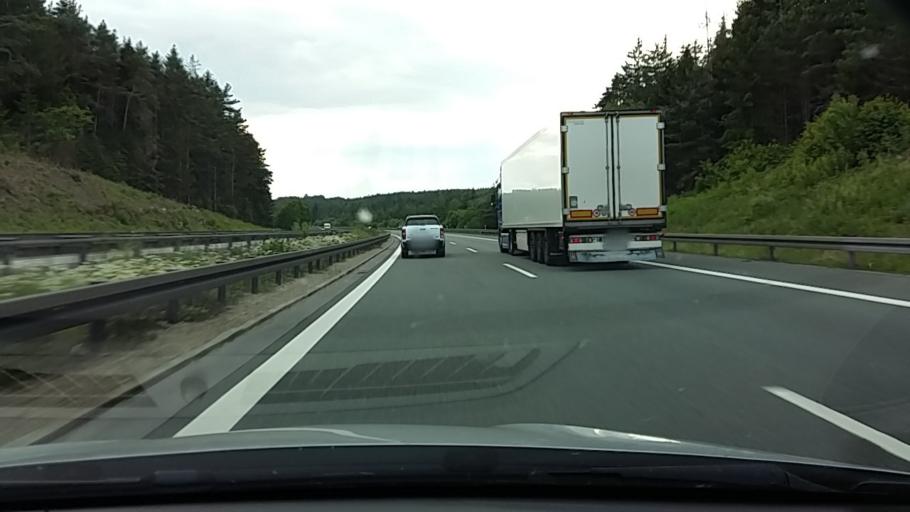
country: DE
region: Bavaria
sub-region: Upper Palatinate
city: Amberg
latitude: 49.4017
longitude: 11.8275
